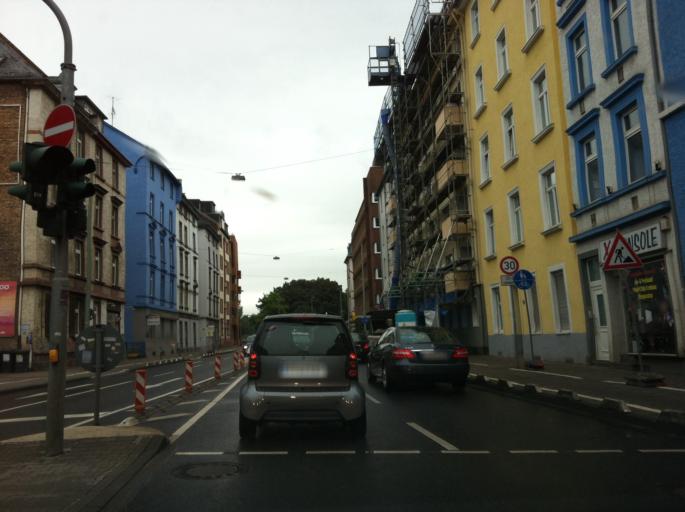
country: DE
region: Hesse
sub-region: Regierungsbezirk Darmstadt
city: Frankfurt am Main
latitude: 50.1241
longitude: 8.7004
